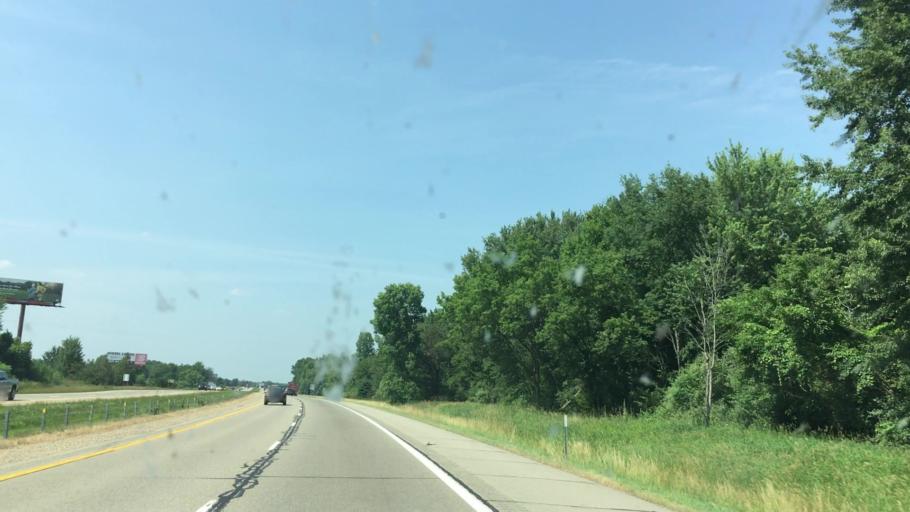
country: US
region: Michigan
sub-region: Allegan County
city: Wayland
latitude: 42.6074
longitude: -85.6598
